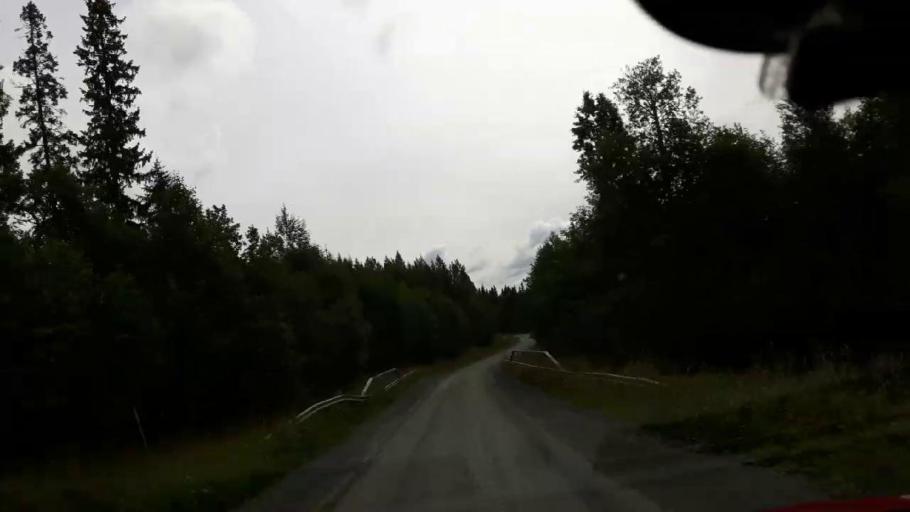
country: SE
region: Jaemtland
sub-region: Krokoms Kommun
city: Valla
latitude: 63.6639
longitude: 13.9674
